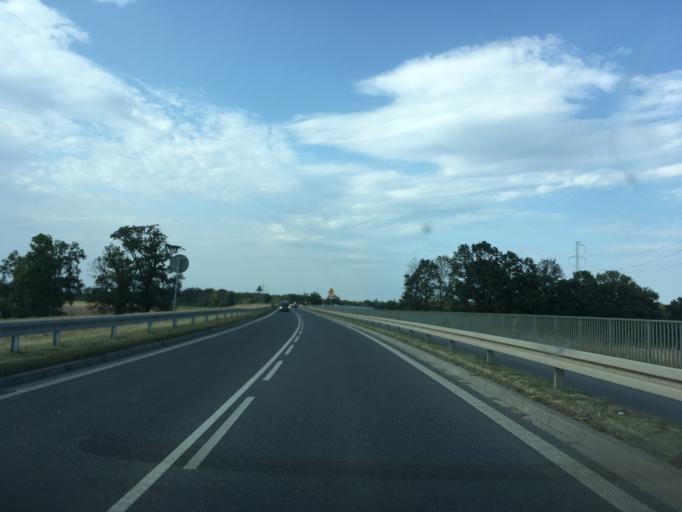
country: PL
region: Lower Silesian Voivodeship
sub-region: Powiat wroclawski
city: Kamieniec Wroclawski
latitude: 51.0690
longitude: 17.1592
